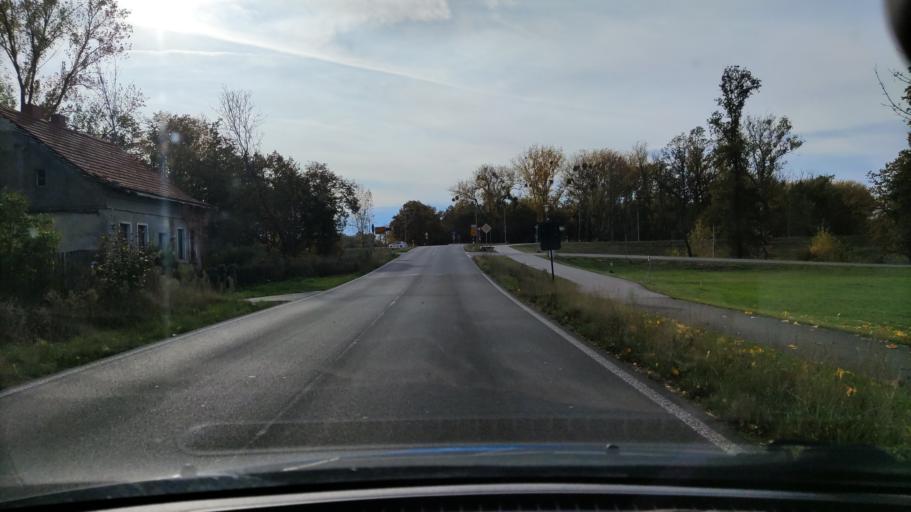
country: DE
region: Brandenburg
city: Breese
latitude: 52.9994
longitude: 11.7847
